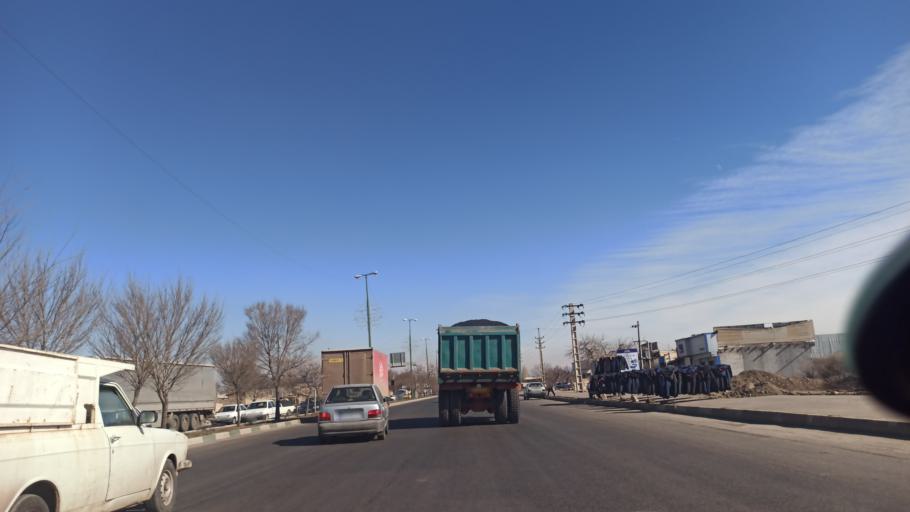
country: IR
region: Qazvin
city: Qazvin
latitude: 36.2563
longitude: 49.9824
